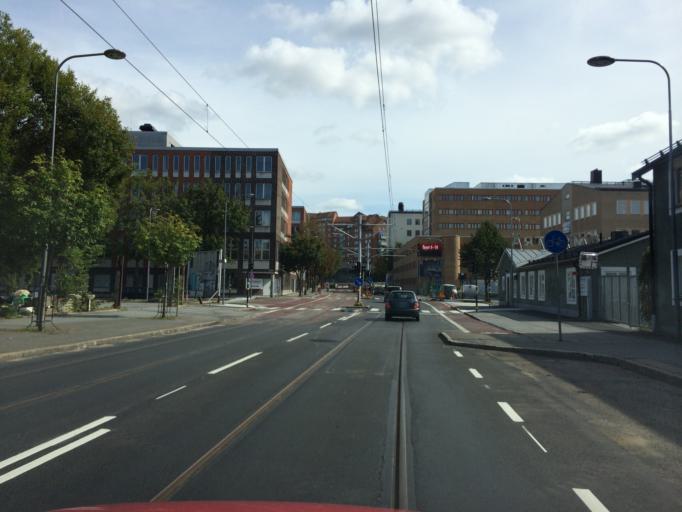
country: SE
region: Stockholm
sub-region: Stockholms Kommun
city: Arsta
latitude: 59.3133
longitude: 18.0215
